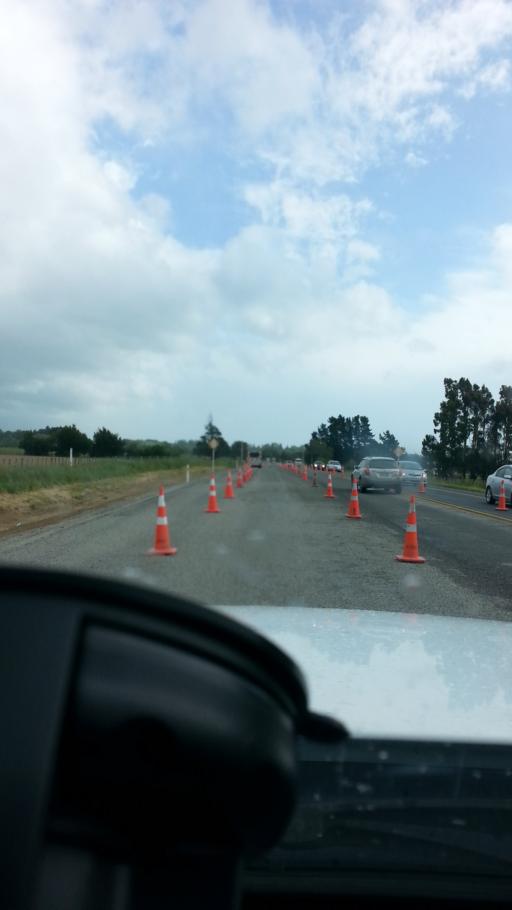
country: NZ
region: Wellington
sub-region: Masterton District
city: Masterton
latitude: -41.0474
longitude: 175.5033
